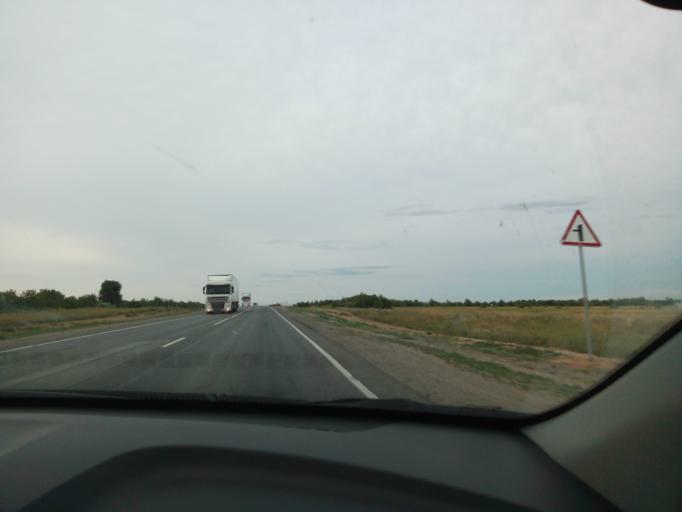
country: RU
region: Volgograd
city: Dubovka
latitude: 49.0348
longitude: 44.7635
